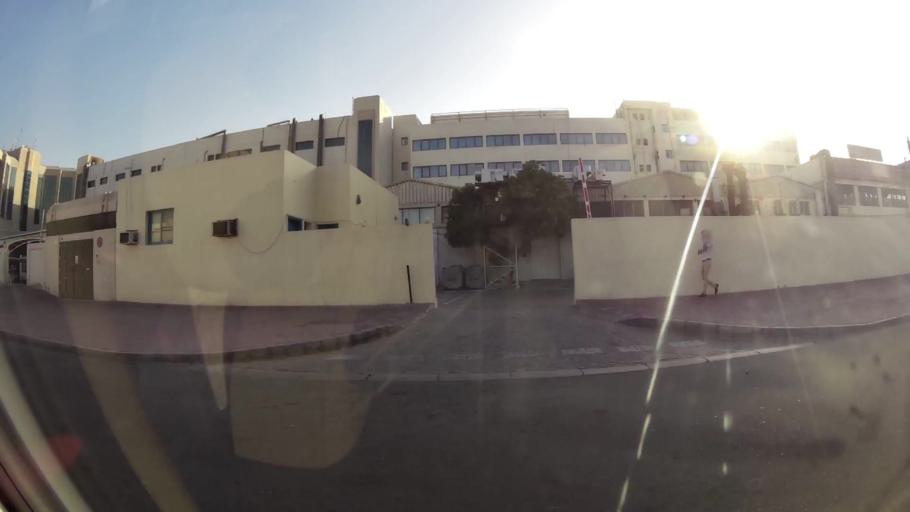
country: AE
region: Ash Shariqah
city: Sharjah
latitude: 25.2492
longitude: 55.3385
